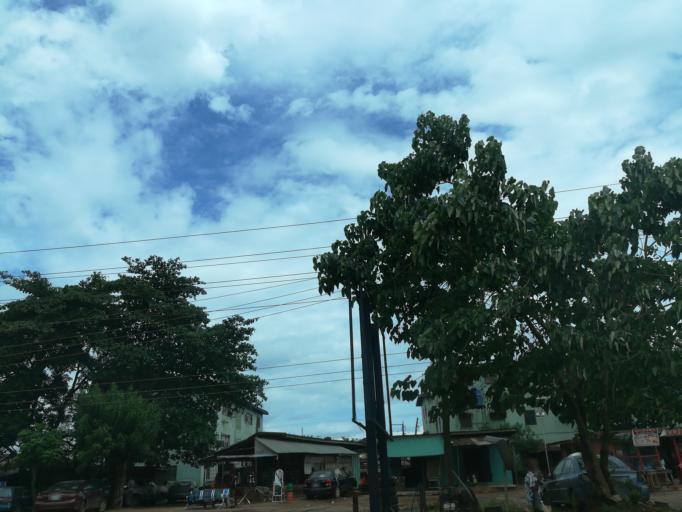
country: NG
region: Lagos
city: Ikorodu
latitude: 6.6323
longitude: 3.5101
